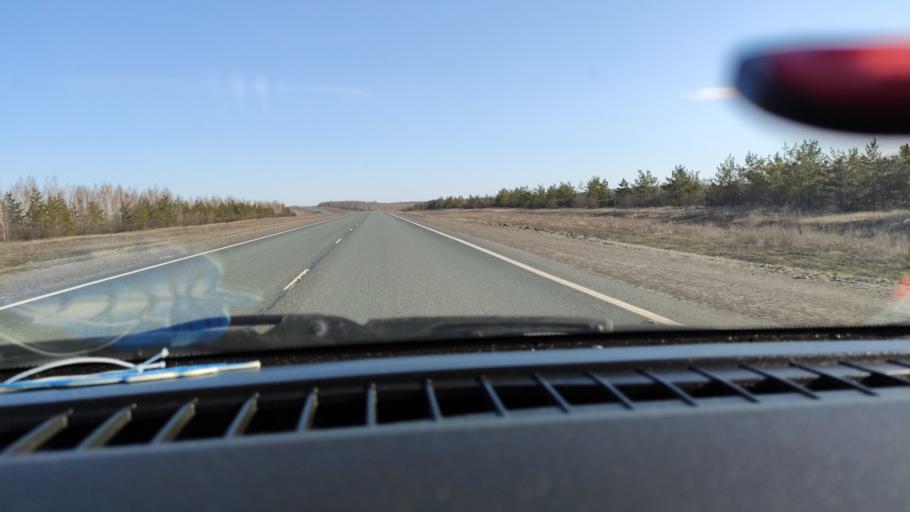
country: RU
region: Samara
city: Syzran'
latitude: 52.8812
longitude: 48.2921
